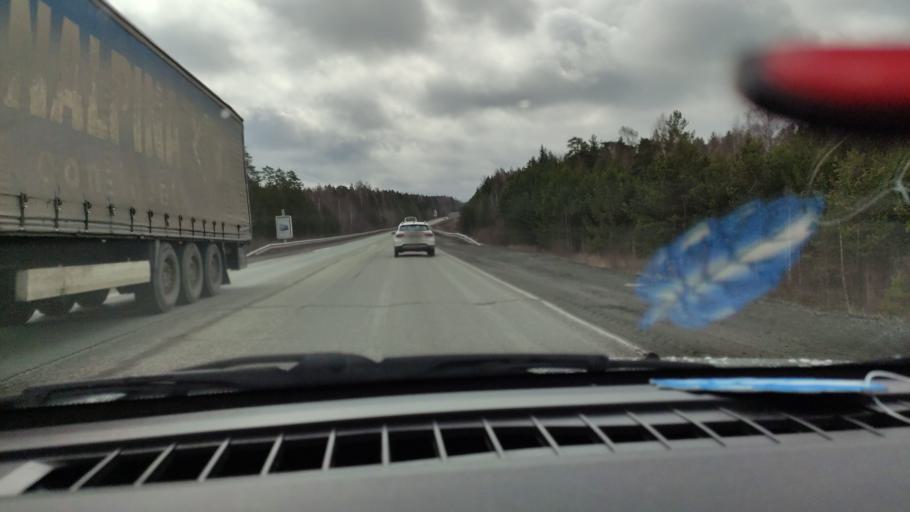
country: RU
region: Sverdlovsk
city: Talitsa
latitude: 56.8632
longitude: 60.0499
